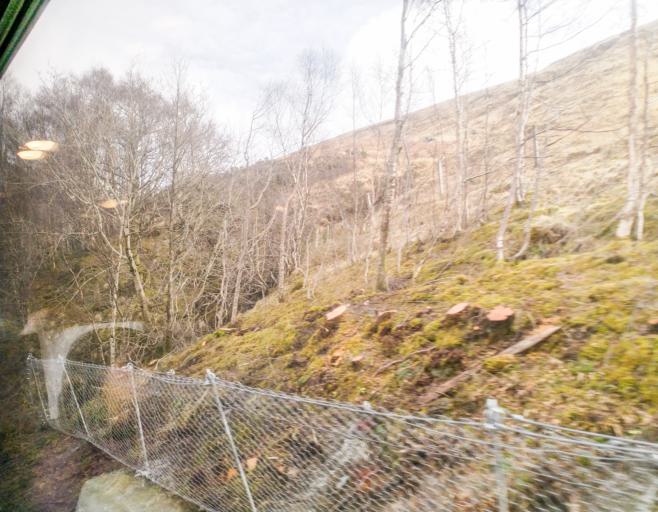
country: GB
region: Scotland
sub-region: Highland
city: Spean Bridge
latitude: 56.8028
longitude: -4.7198
